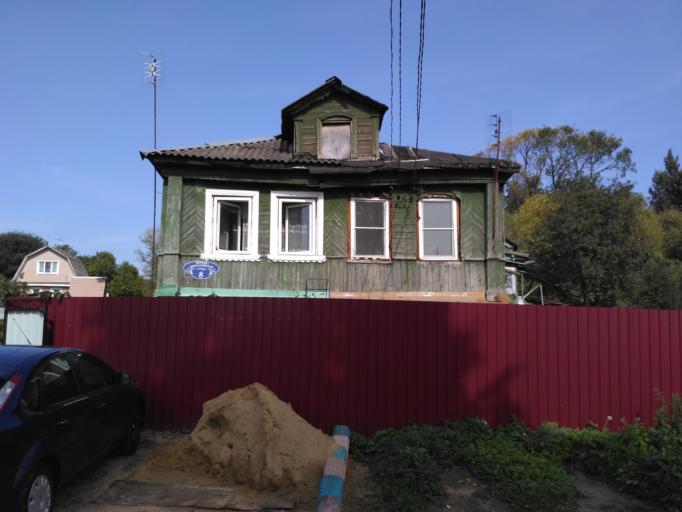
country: RU
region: Moskovskaya
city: Sergiyev Posad
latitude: 56.3048
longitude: 38.1202
